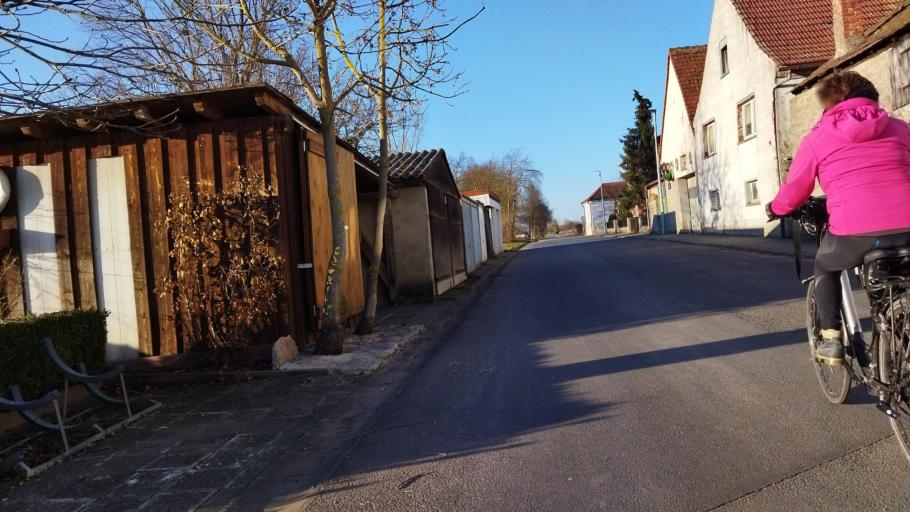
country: DE
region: Bavaria
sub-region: Regierungsbezirk Unterfranken
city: Albertshofen
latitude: 49.7726
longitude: 10.1577
